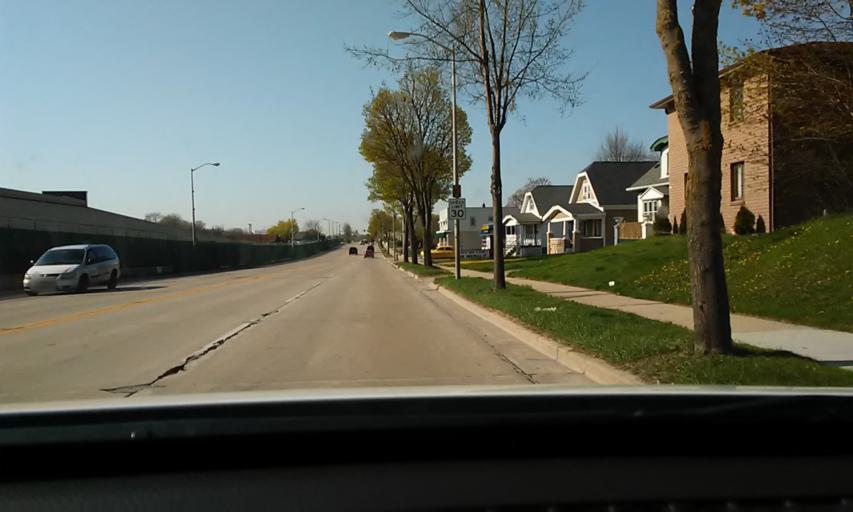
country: US
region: Wisconsin
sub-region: Milwaukee County
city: West Allis
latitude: 43.0227
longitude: -88.0173
